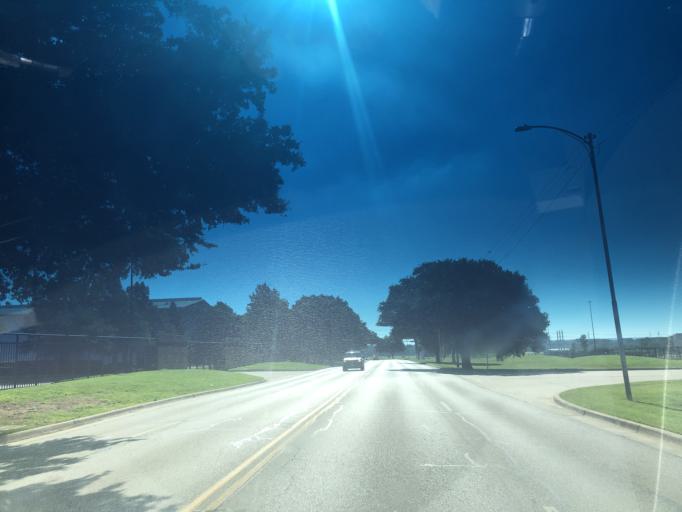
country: US
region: Texas
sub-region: Dallas County
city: Grand Prairie
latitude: 32.7205
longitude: -97.0315
